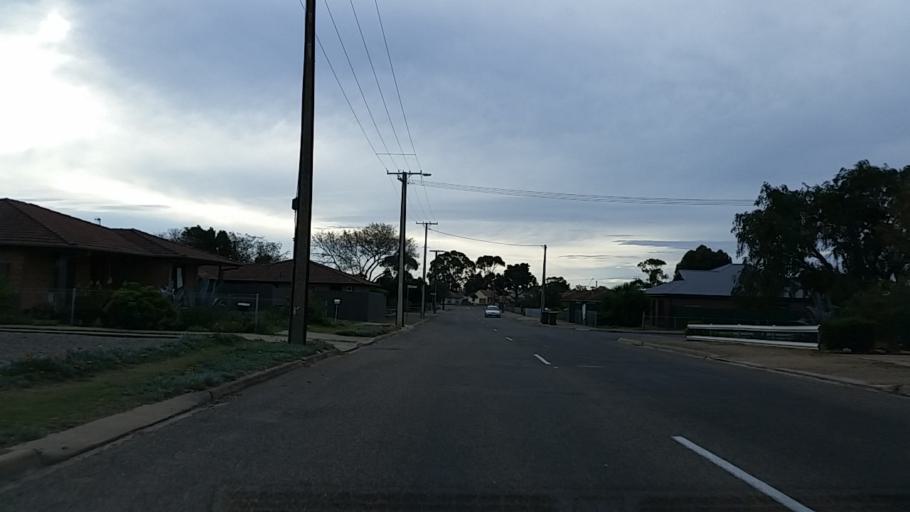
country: AU
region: South Australia
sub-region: Murray Bridge
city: Murray Bridge
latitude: -35.1317
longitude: 139.2791
